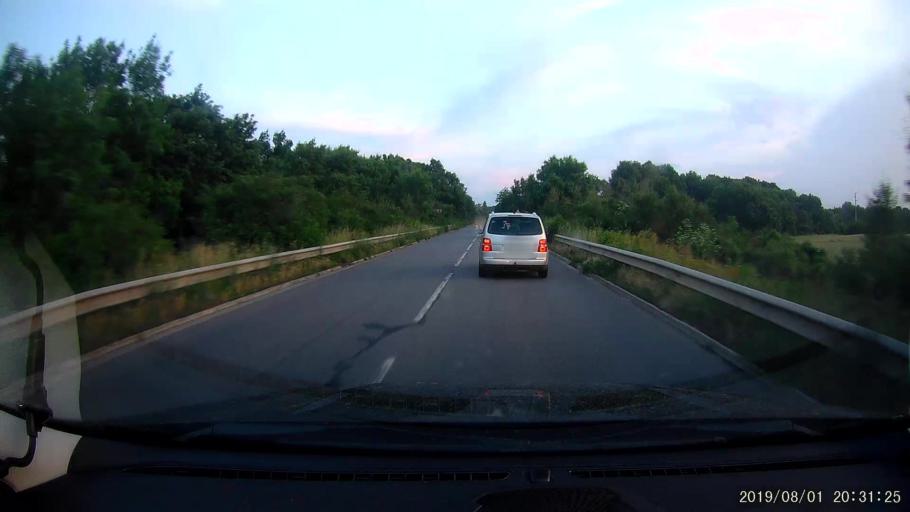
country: BG
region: Yambol
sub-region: Obshtina Elkhovo
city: Elkhovo
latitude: 42.1288
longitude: 26.5398
